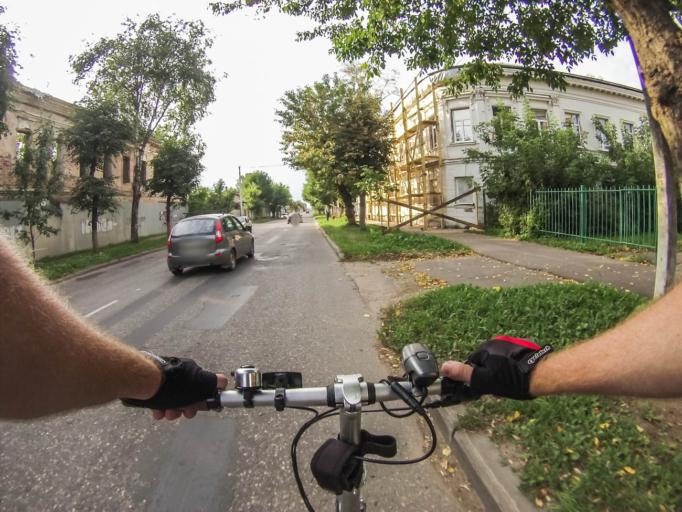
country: RU
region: Kostroma
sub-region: Kostromskoy Rayon
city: Kostroma
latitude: 57.7732
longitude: 40.9110
